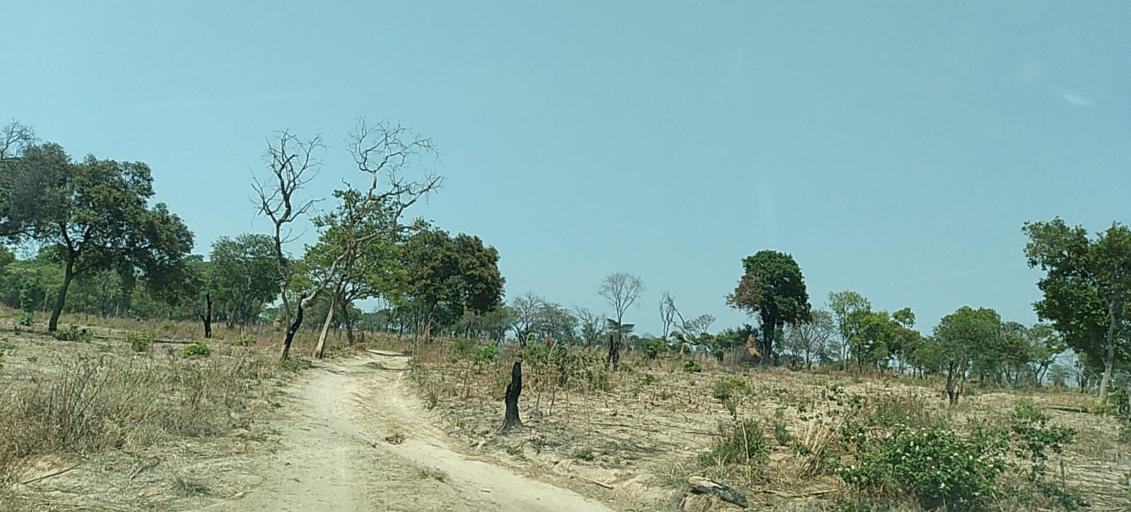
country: ZM
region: Copperbelt
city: Mpongwe
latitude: -13.8559
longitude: 28.0566
